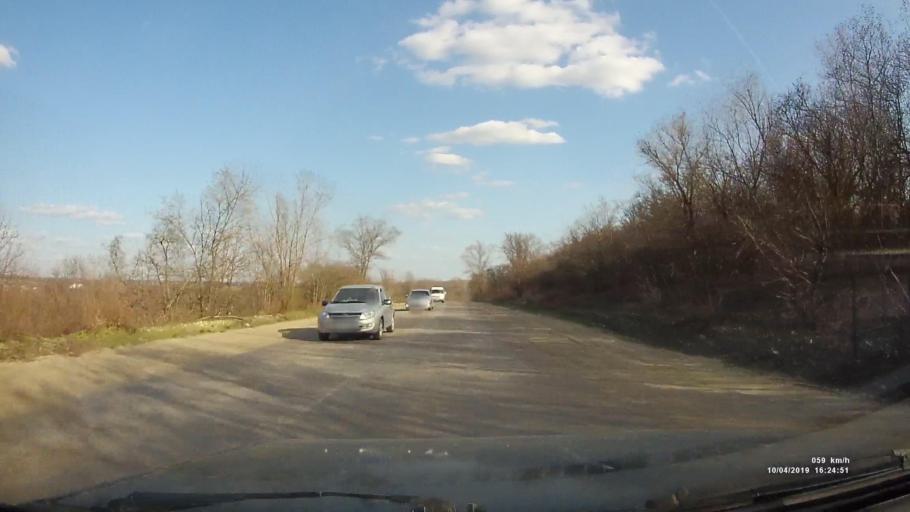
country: RU
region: Rostov
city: Staraya Stanitsa
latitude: 48.2966
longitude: 40.3179
